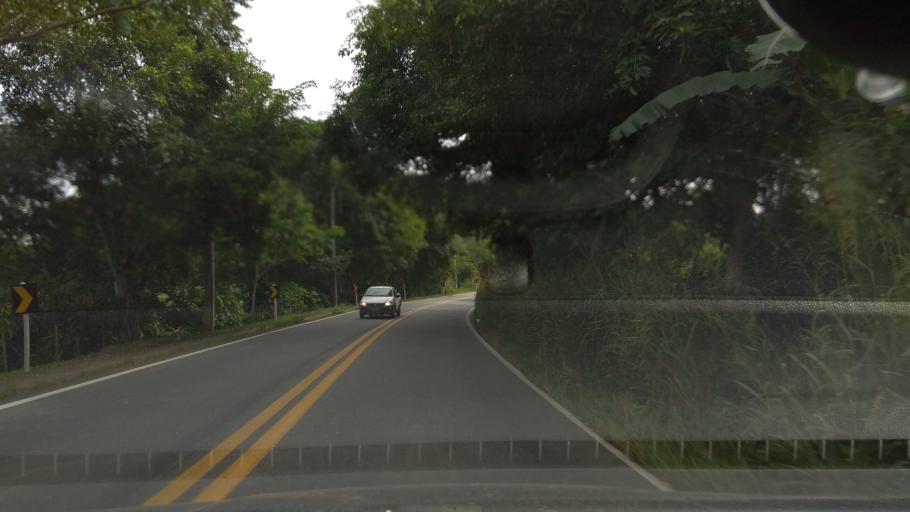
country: BR
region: Bahia
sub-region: Ubata
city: Ubata
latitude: -14.1944
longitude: -39.5549
